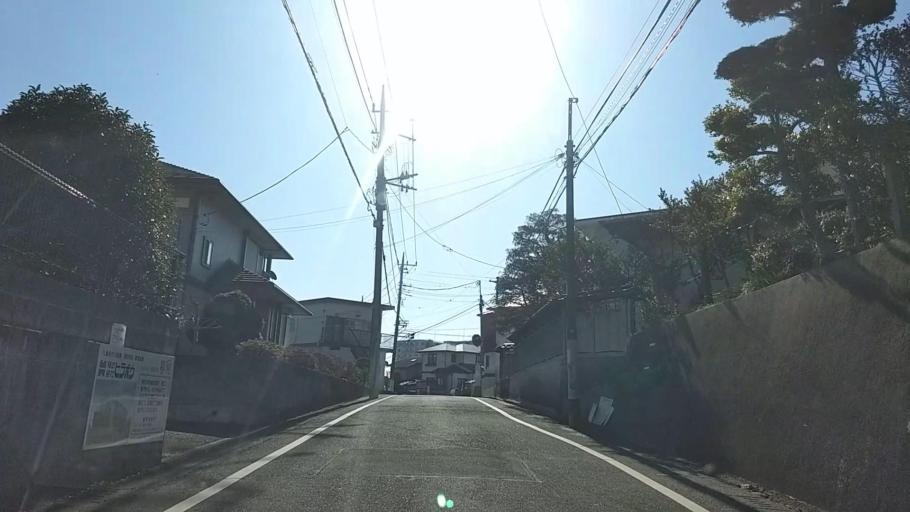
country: JP
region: Kanagawa
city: Hadano
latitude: 35.3791
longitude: 139.2263
